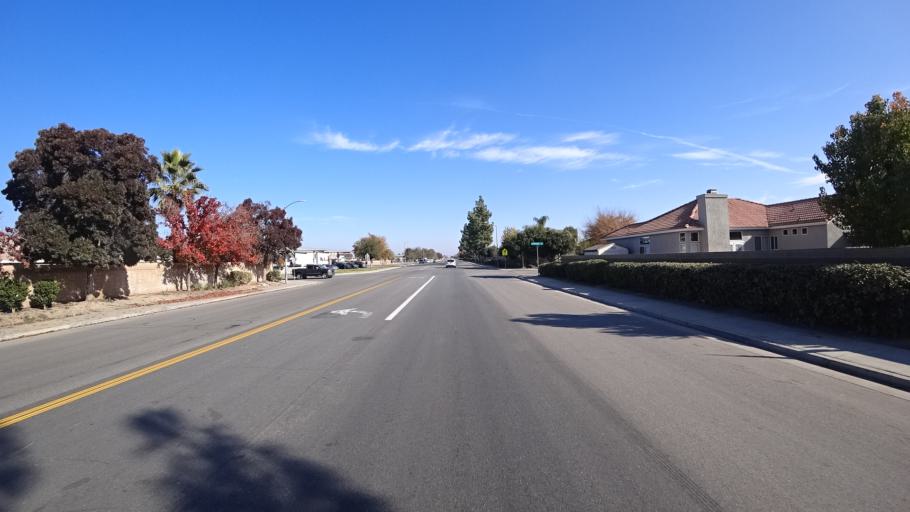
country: US
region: California
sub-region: Kern County
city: Greenfield
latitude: 35.2886
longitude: -119.0469
